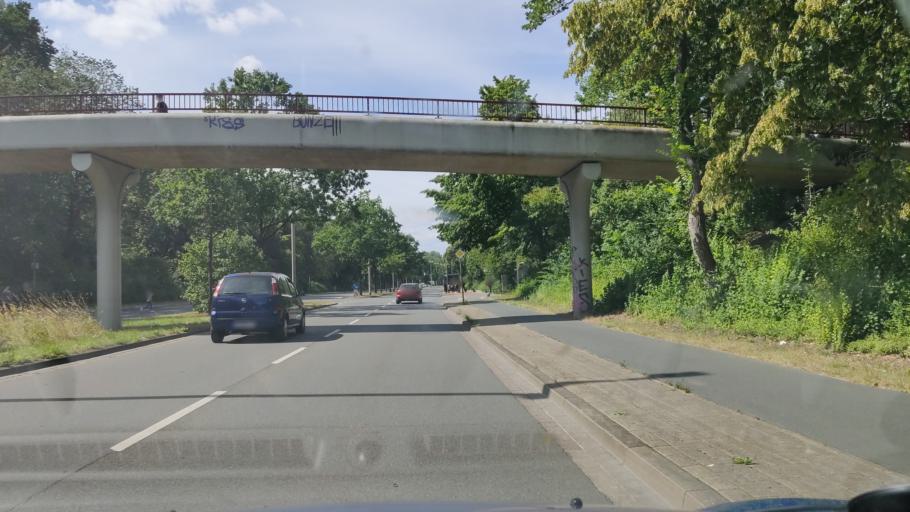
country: DE
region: Lower Saxony
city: Hemmingen
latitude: 52.3439
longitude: 9.6930
